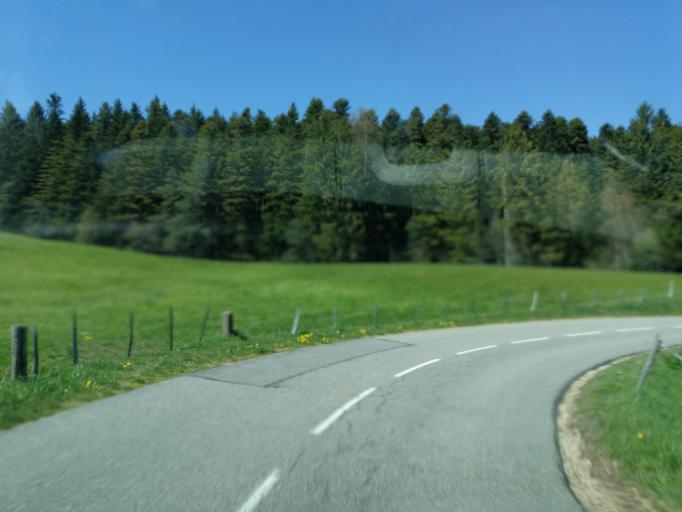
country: FR
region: Rhone-Alpes
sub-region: Departement de la Loire
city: Marlhes
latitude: 45.2884
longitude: 4.3853
